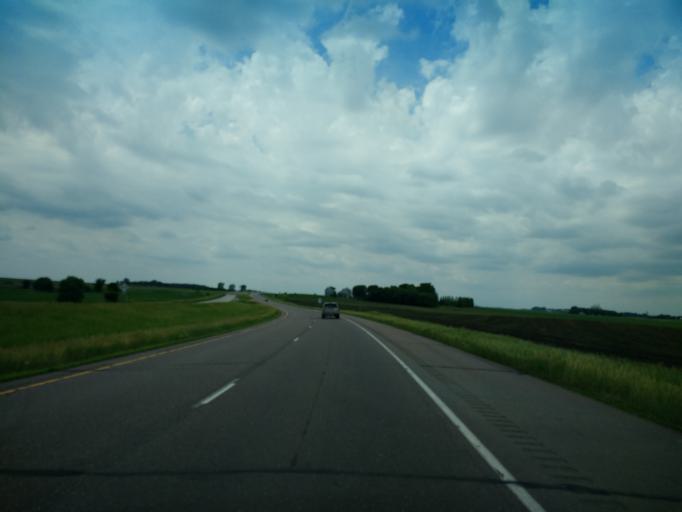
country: US
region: Minnesota
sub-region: Cottonwood County
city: Mountain Lake
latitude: 43.9324
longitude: -94.9538
